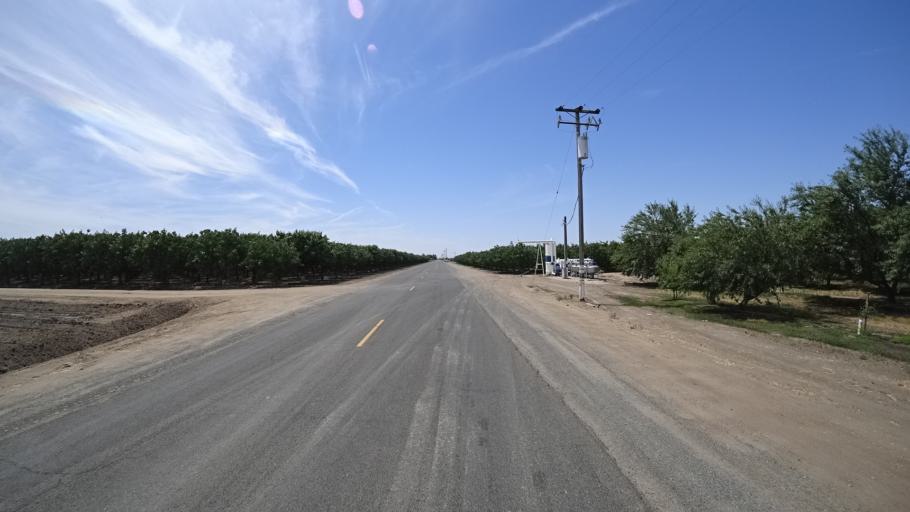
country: US
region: California
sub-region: Kings County
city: Lucerne
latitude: 36.3973
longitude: -119.6910
